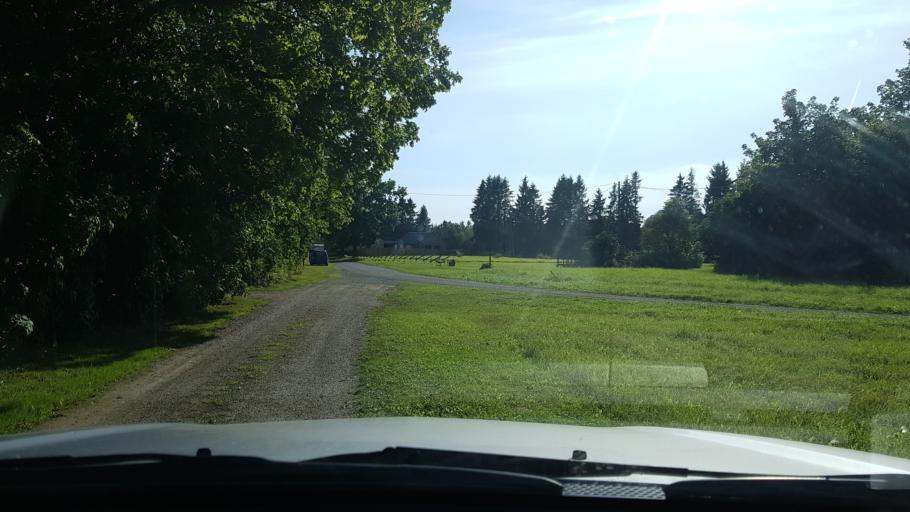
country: EE
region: Ida-Virumaa
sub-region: Narva-Joesuu linn
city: Narva-Joesuu
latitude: 59.4040
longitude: 28.0028
